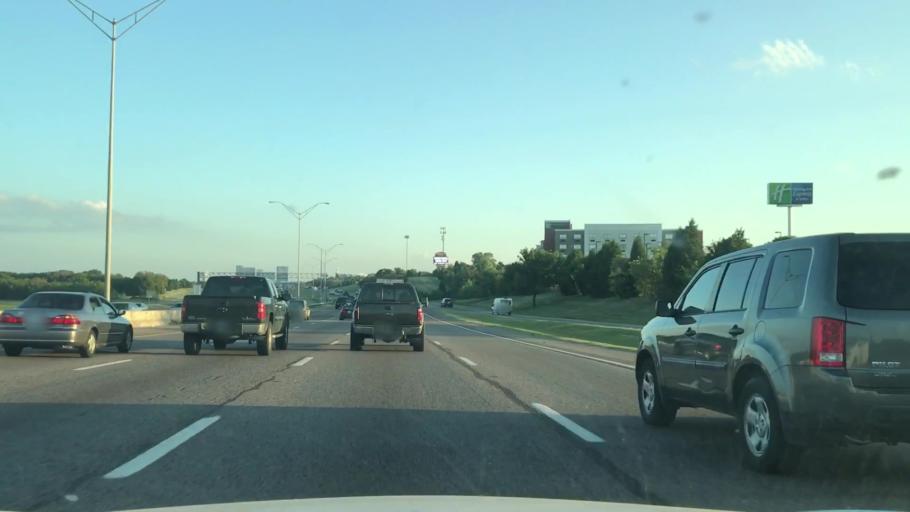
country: US
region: Texas
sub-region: Dallas County
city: Mesquite
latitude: 32.7667
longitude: -96.6220
